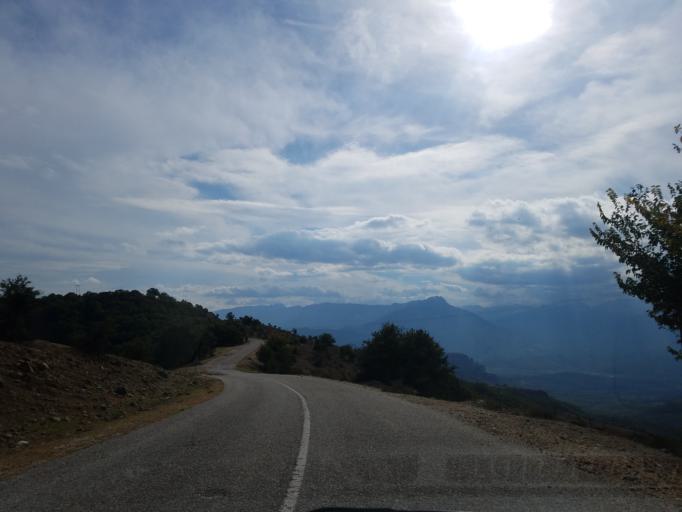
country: GR
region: Thessaly
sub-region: Trikala
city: Kastraki
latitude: 39.7565
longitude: 21.6623
